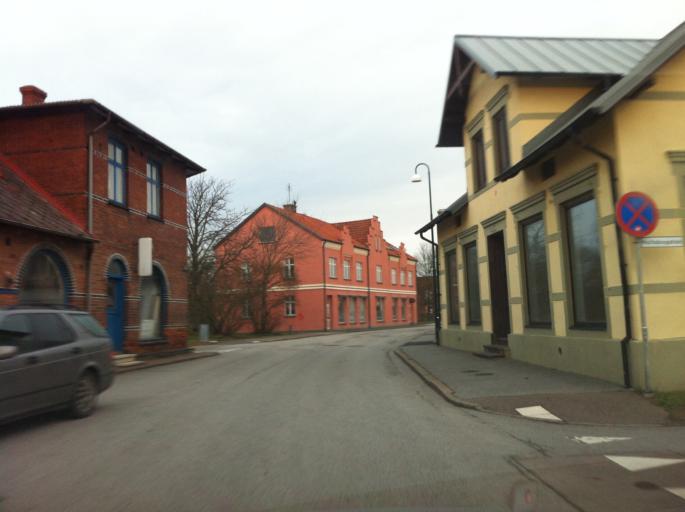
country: SE
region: Skane
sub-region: Hoganas Kommun
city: Hoganas
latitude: 56.2040
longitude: 12.5512
